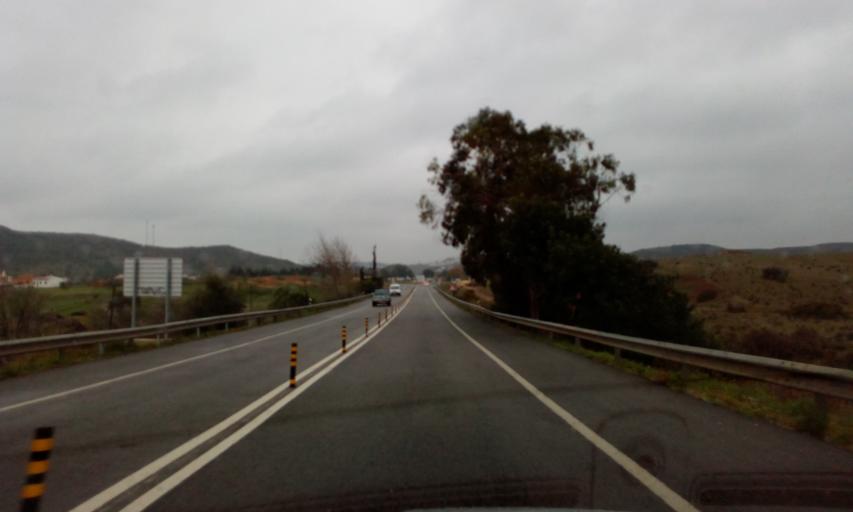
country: PT
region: Faro
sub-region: Vila do Bispo
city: Vila do Bispo
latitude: 37.0934
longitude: -8.8087
